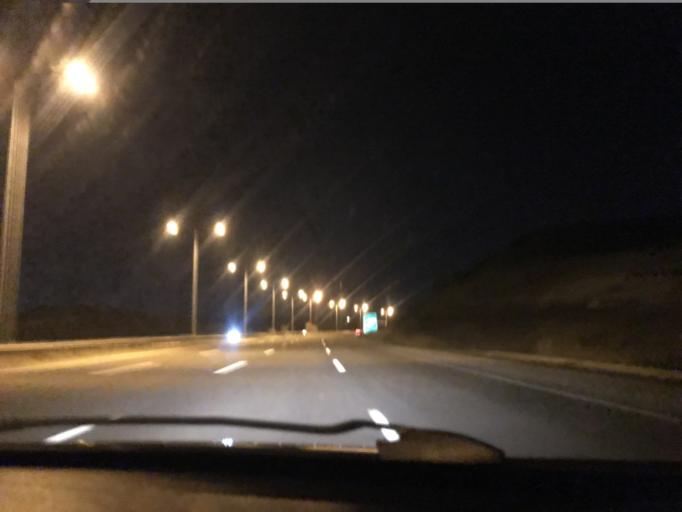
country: TR
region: Ankara
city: Etimesgut
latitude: 39.8793
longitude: 32.6253
